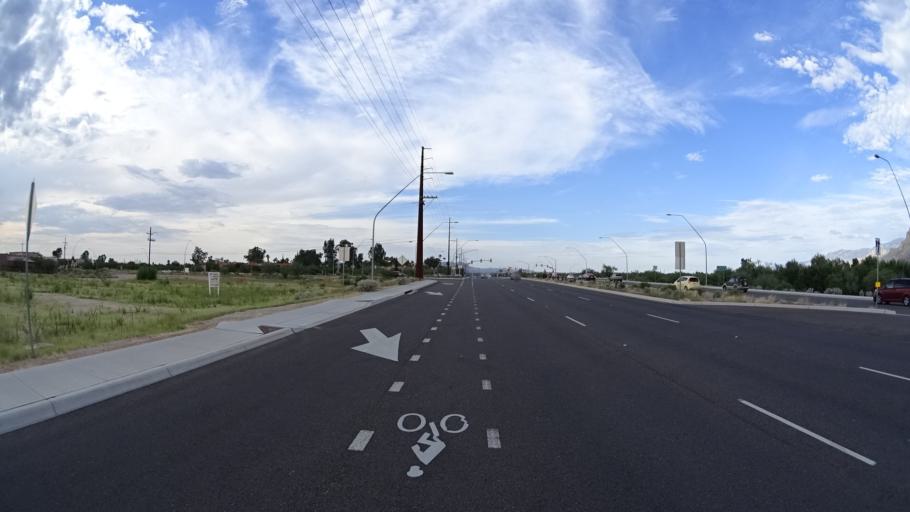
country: US
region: Arizona
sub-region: Pima County
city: Casas Adobes
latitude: 32.3463
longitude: -111.0128
